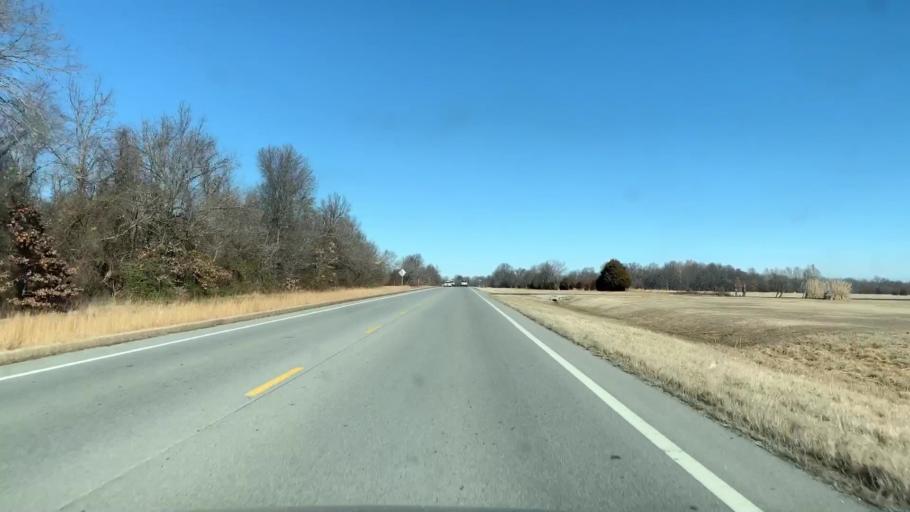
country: US
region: Kansas
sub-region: Cherokee County
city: Baxter Springs
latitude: 37.0437
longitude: -94.7355
